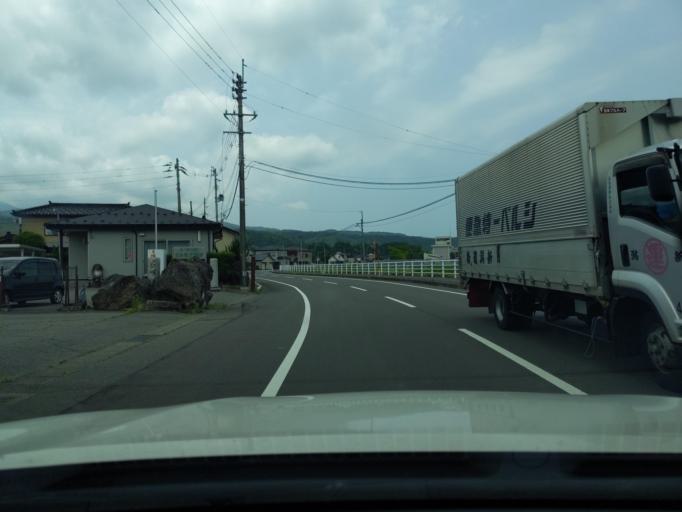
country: JP
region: Niigata
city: Kashiwazaki
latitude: 37.3303
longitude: 138.5705
